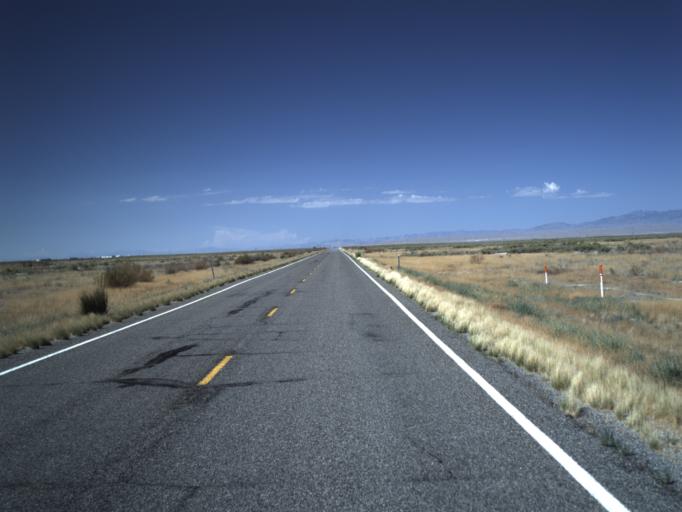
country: US
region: Utah
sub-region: Millard County
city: Delta
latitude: 39.2944
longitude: -112.8217
